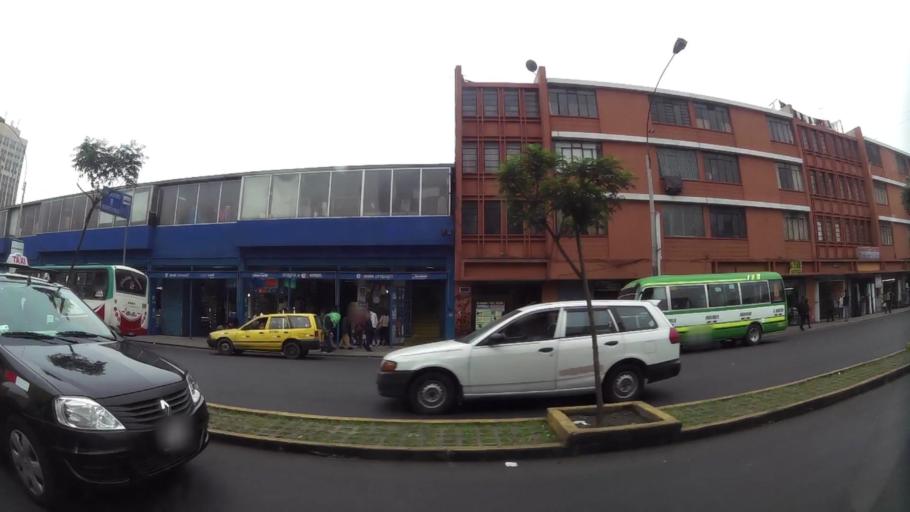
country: PE
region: Lima
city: Lima
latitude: -12.0572
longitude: -77.0304
